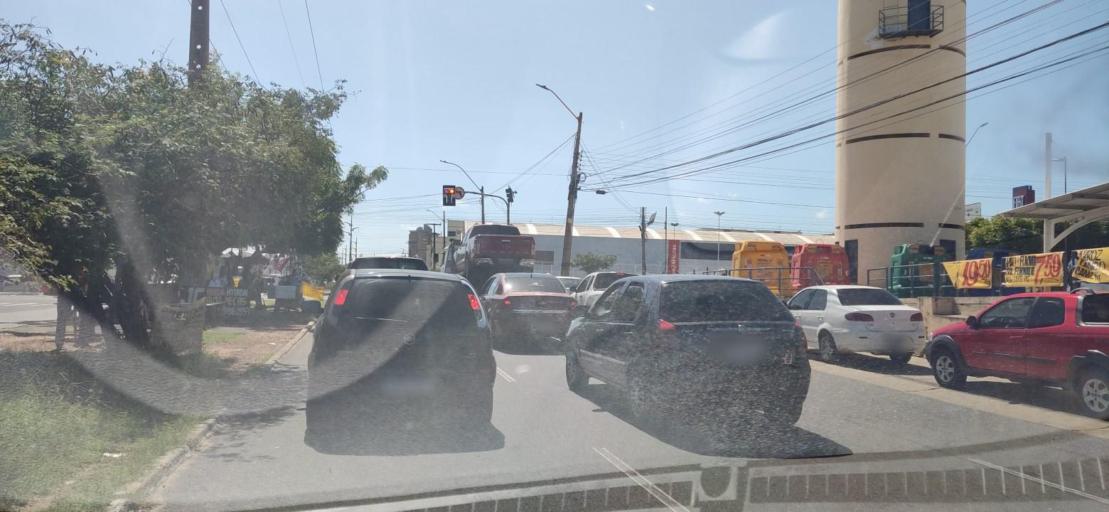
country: BR
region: Piaui
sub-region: Teresina
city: Teresina
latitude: -5.1198
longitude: -42.8035
